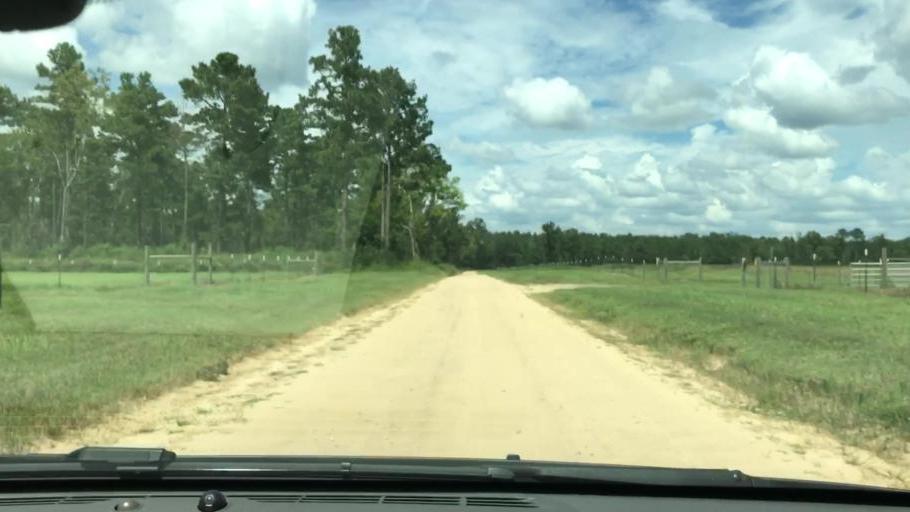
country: US
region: Georgia
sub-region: Quitman County
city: Georgetown
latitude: 32.0329
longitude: -85.0366
